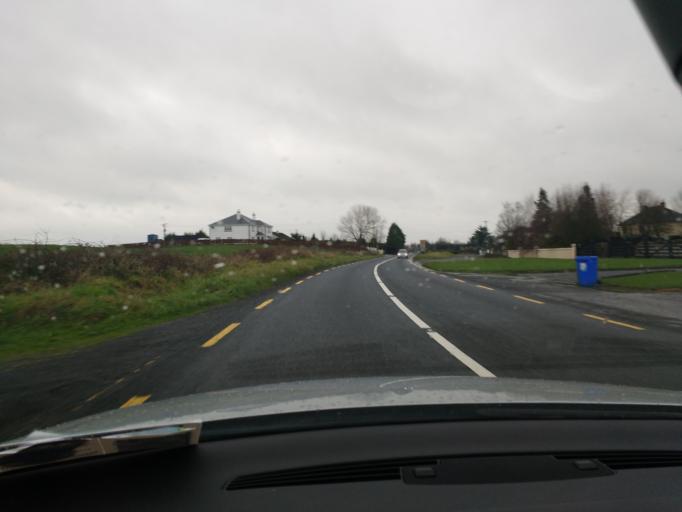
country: IE
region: Munster
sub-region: North Tipperary
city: Nenagh
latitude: 52.8329
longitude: -8.1225
